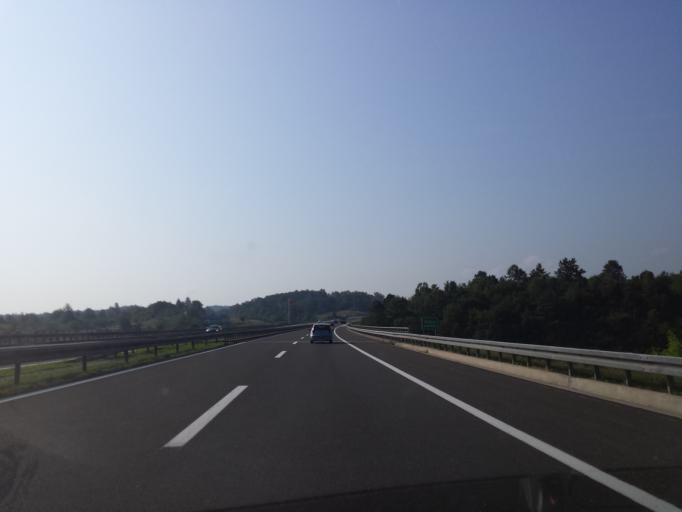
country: HR
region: Karlovacka
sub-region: Grad Ogulin
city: Ogulin
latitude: 45.3263
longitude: 15.2805
